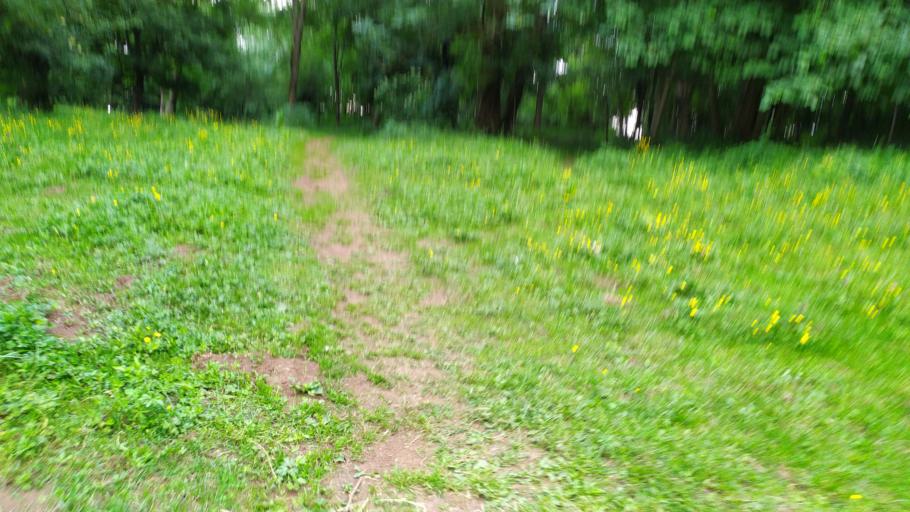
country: IT
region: Veneto
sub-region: Provincia di Vicenza
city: Torrebelvicino
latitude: 45.6777
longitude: 11.3191
